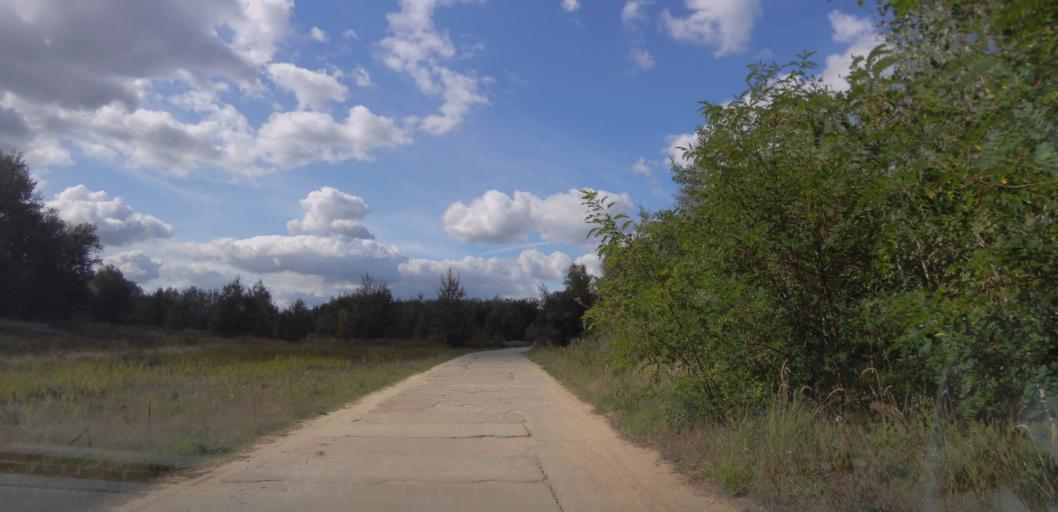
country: PL
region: Subcarpathian Voivodeship
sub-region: Tarnobrzeg
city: Tarnobrzeg
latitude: 50.5329
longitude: 21.6603
